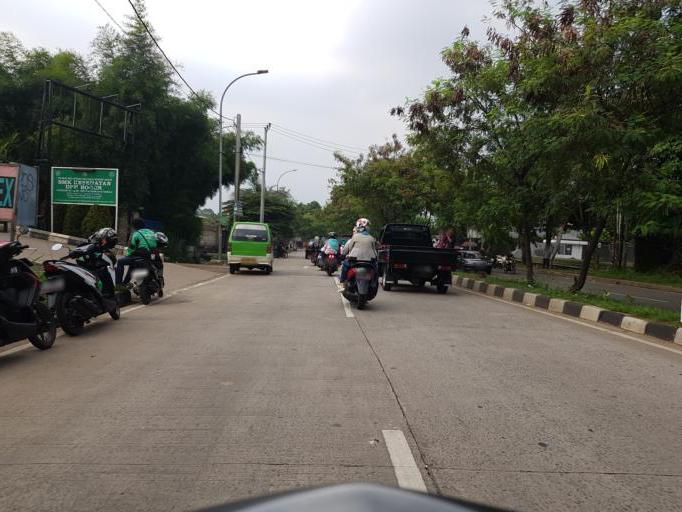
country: ID
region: West Java
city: Bogor
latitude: -6.5308
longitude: 106.7665
